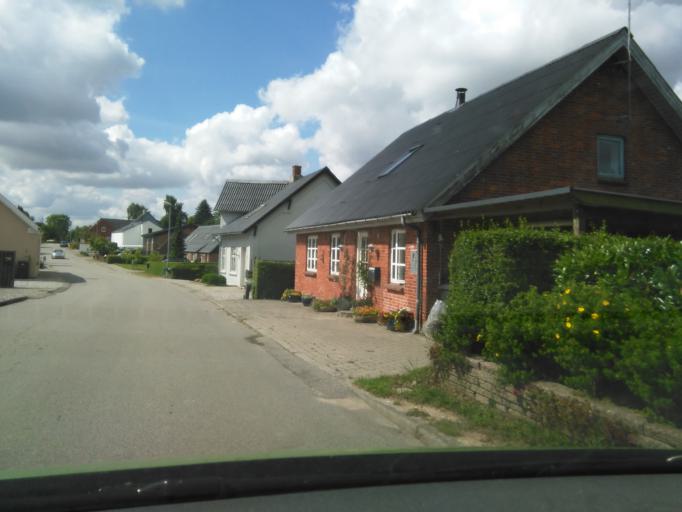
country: DK
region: Central Jutland
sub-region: Arhus Kommune
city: Solbjerg
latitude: 55.9820
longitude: 10.0564
